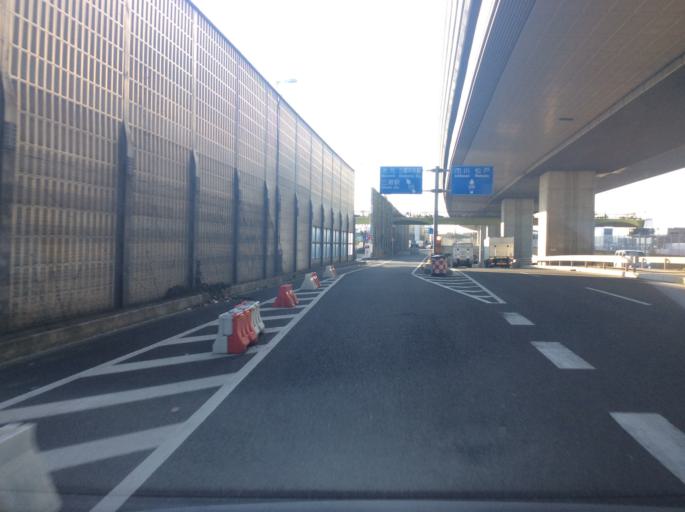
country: JP
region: Saitama
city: Yashio-shi
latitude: 35.8275
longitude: 139.8693
